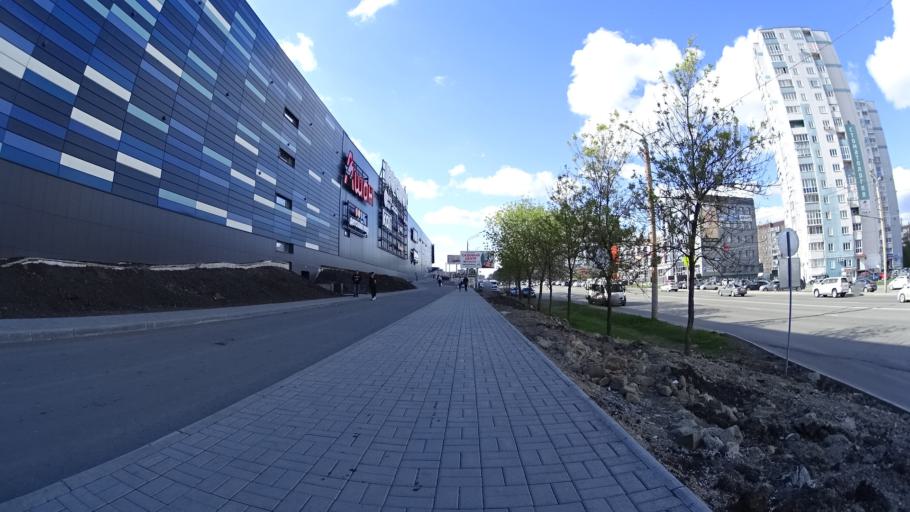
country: RU
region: Chelyabinsk
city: Roshchino
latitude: 55.1809
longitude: 61.2941
